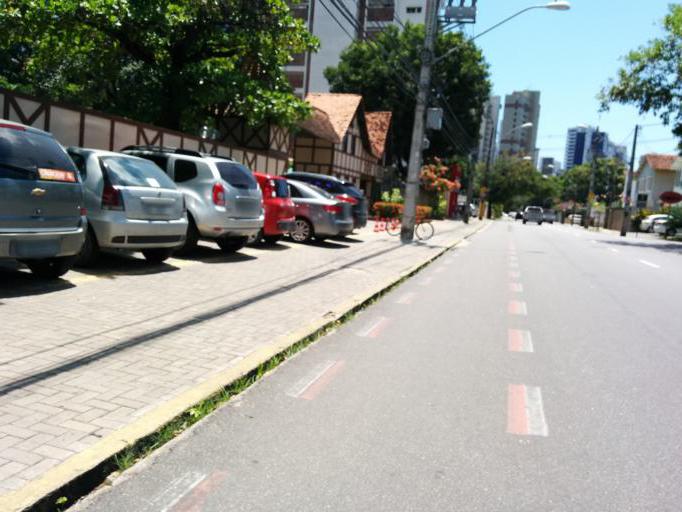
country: BR
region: Pernambuco
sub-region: Recife
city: Recife
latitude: -8.0325
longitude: -34.9122
